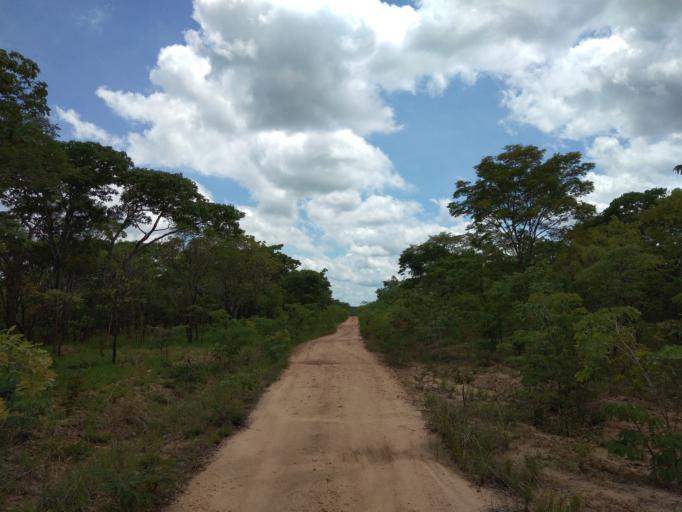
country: ZM
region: Central
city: Mkushi
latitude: -13.9934
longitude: 29.9538
